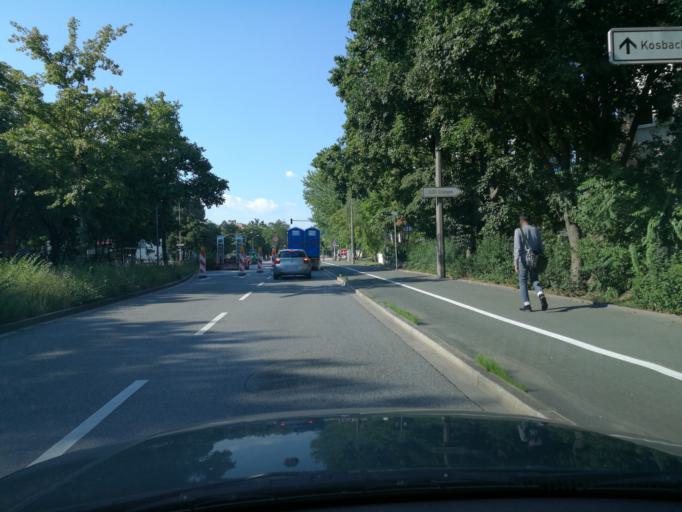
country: DE
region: Bavaria
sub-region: Regierungsbezirk Mittelfranken
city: Erlangen
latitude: 49.5888
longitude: 10.9697
